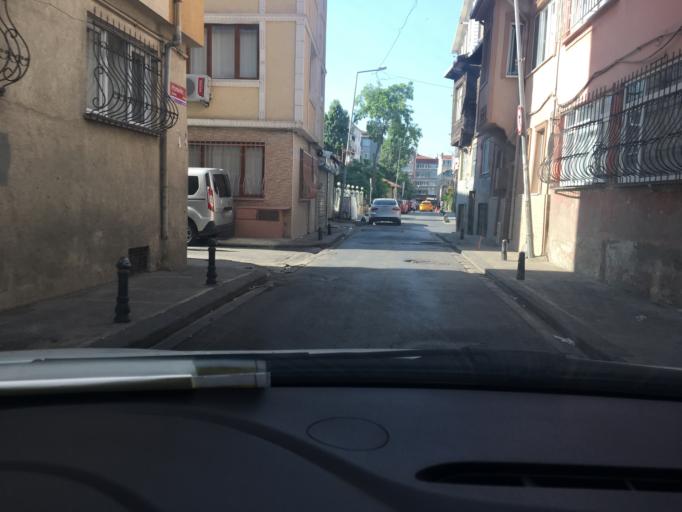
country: TR
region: Istanbul
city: Eminoenue
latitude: 41.0372
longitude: 28.9679
